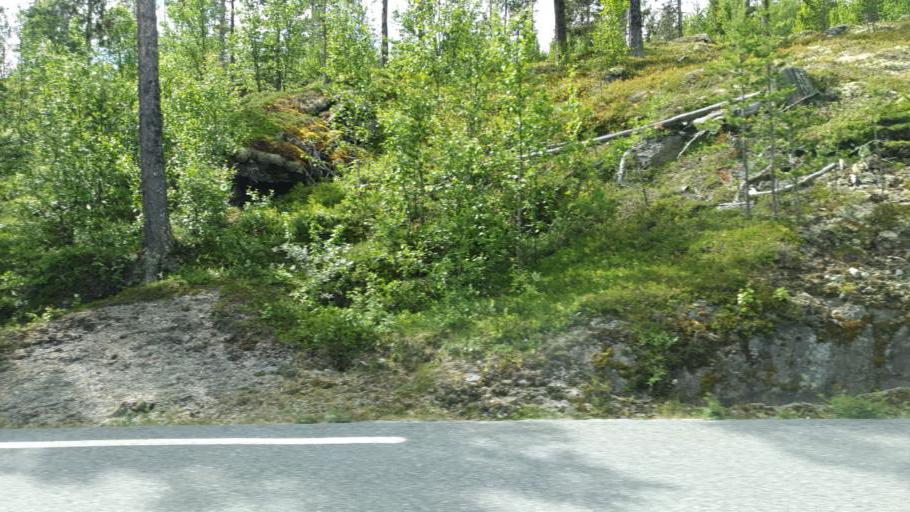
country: NO
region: Oppland
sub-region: Vaga
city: Vagamo
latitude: 61.7461
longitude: 9.0875
